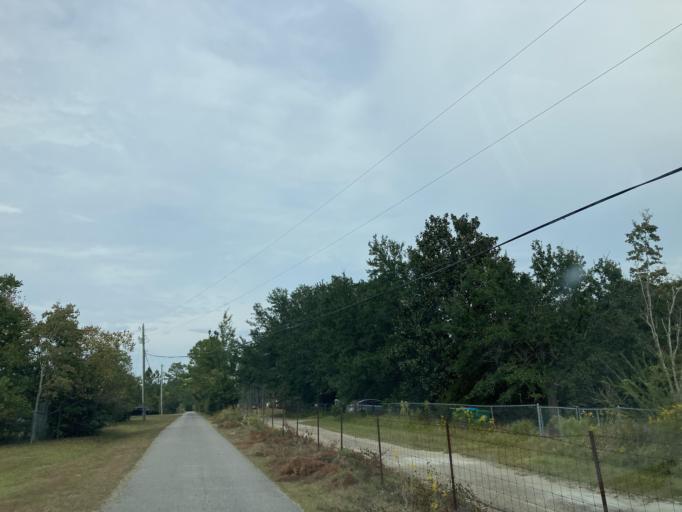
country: US
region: Mississippi
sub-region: Jackson County
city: Saint Martin
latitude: 30.4651
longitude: -88.8602
